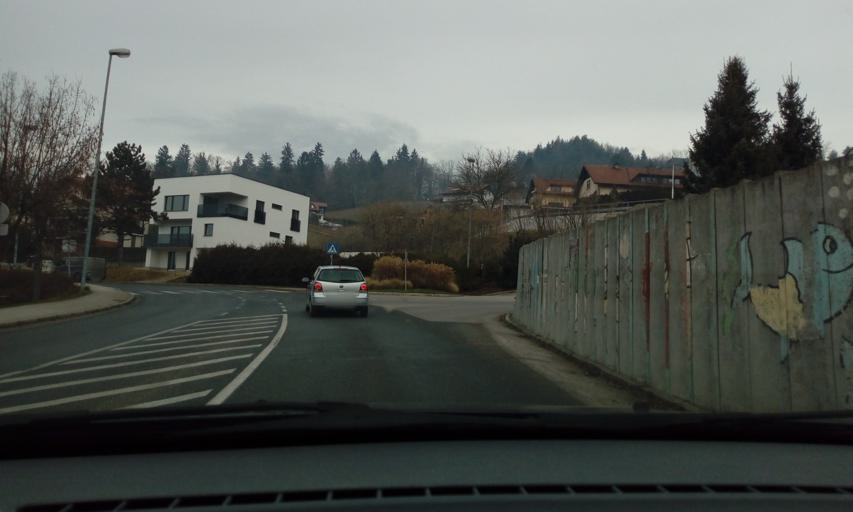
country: SI
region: Sentjur pri Celju
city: Sentjur
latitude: 46.2143
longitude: 15.3994
